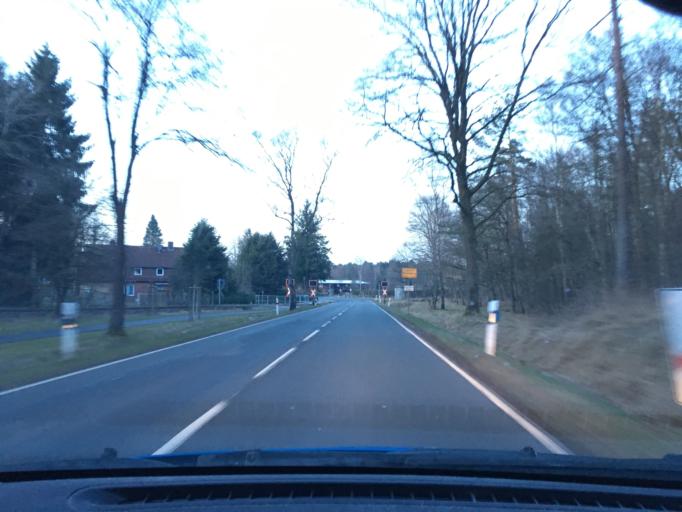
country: DE
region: Lower Saxony
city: Egestorf
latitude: 53.1777
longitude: 10.0629
